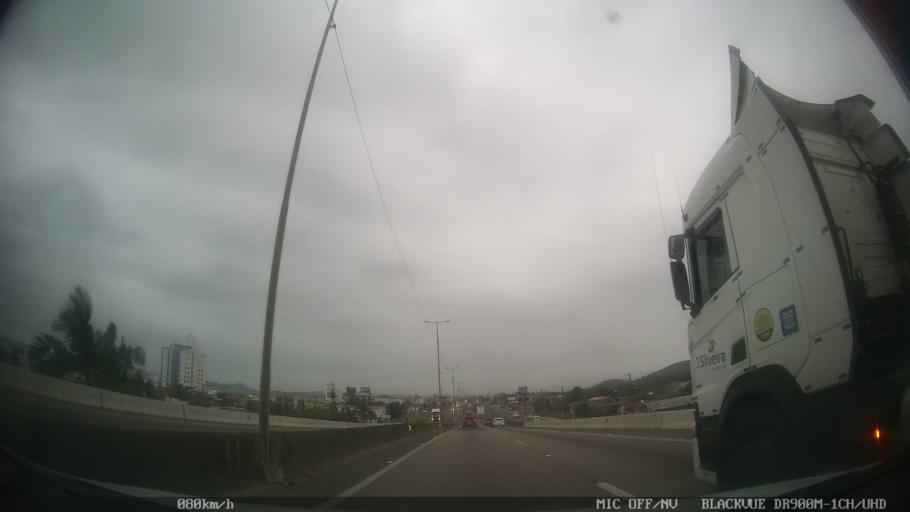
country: BR
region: Santa Catarina
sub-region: Barra Velha
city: Barra Velha
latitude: -26.6517
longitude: -48.6869
